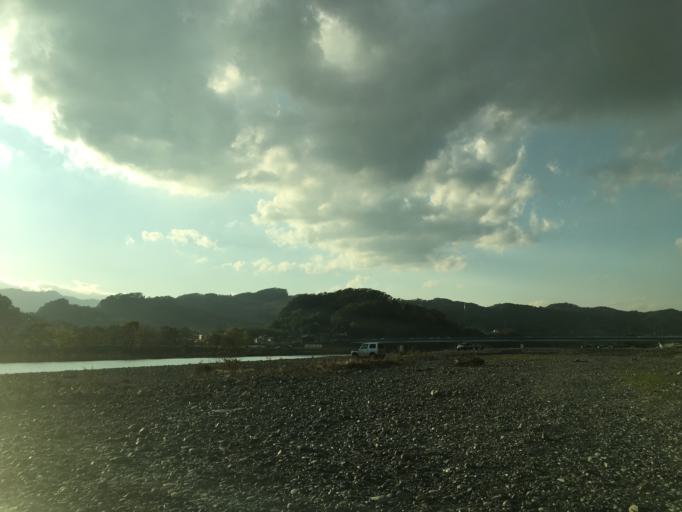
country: JP
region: Kanagawa
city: Zama
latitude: 35.5389
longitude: 139.3360
